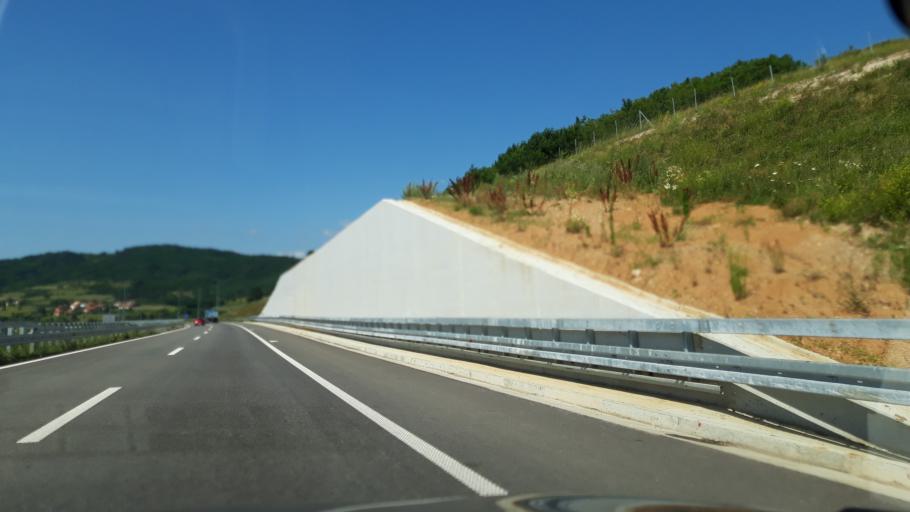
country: RS
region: Central Serbia
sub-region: Pcinjski Okrug
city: Vladicin Han
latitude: 42.7169
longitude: 22.0752
